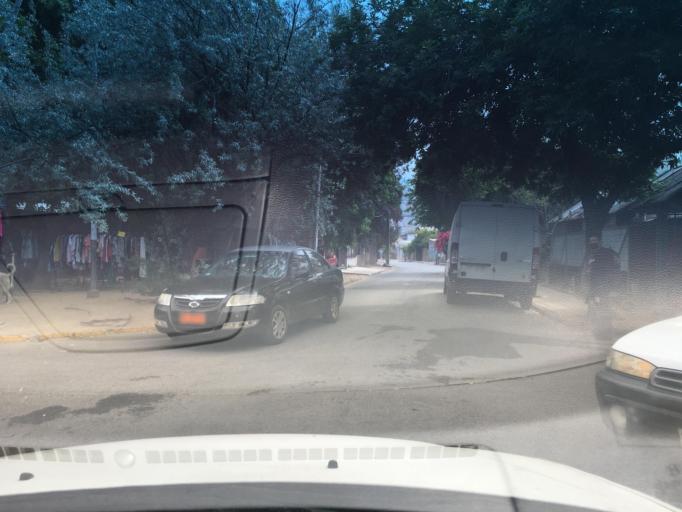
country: CL
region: Santiago Metropolitan
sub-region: Provincia de Santiago
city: Santiago
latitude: -33.3842
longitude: -70.6452
